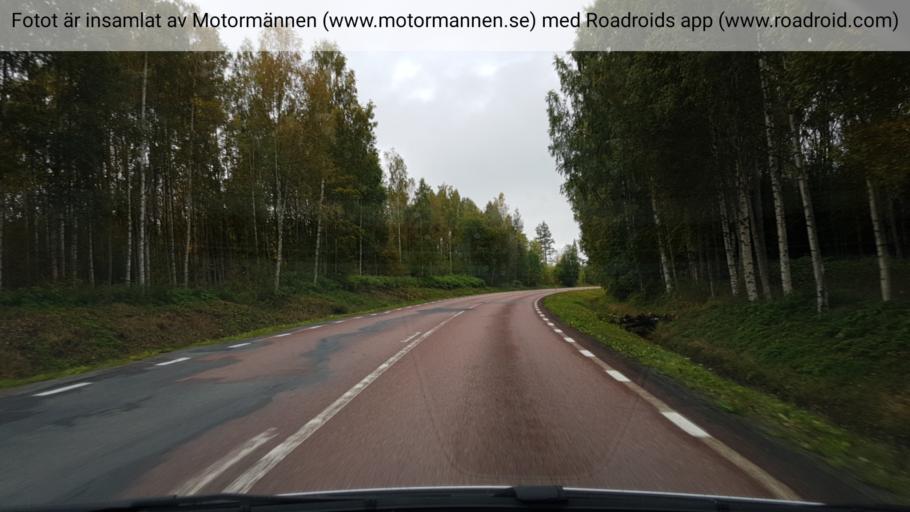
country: SE
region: Jaemtland
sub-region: Stroemsunds Kommun
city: Stroemsund
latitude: 63.9936
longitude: 15.8899
